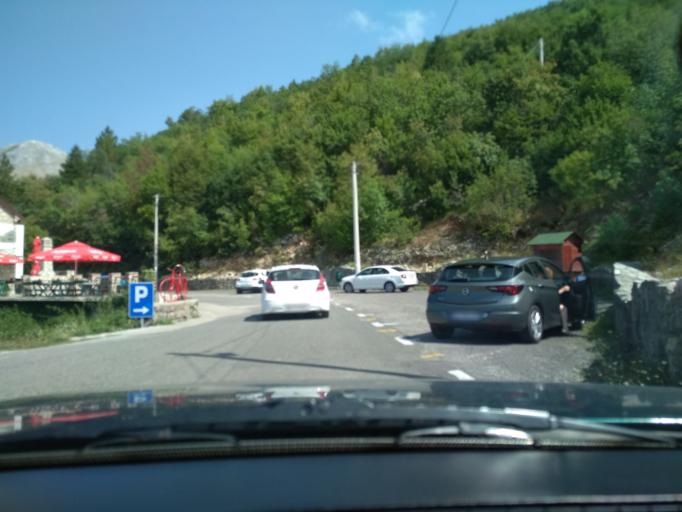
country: ME
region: Kotor
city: Kotor
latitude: 42.4195
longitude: 18.7944
